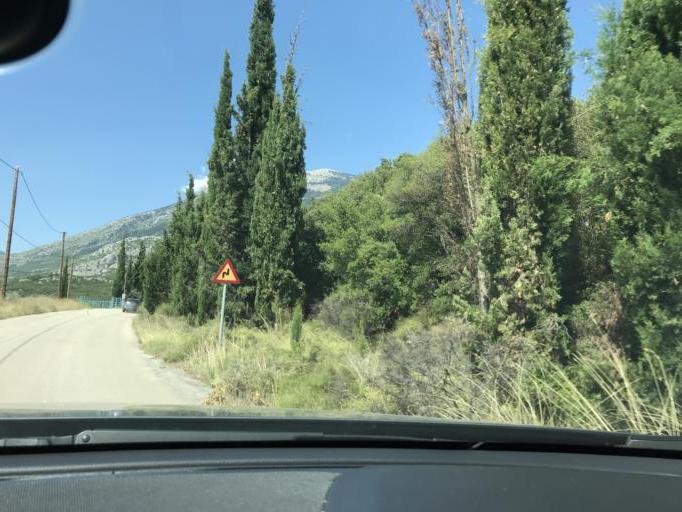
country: GR
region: Central Greece
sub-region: Nomos Voiotias
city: Distomo
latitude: 38.5106
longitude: 22.7190
